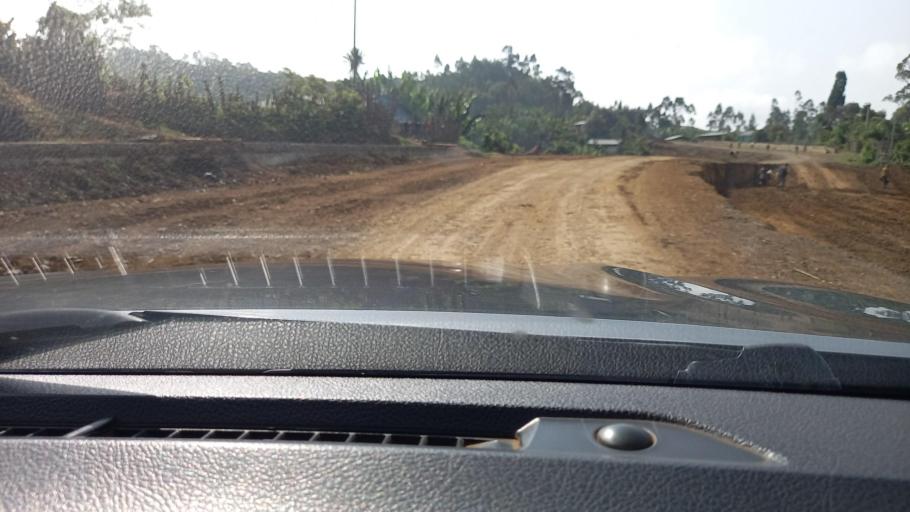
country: ET
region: Southern Nations, Nationalities, and People's Region
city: Mizan Teferi
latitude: 6.1645
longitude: 35.5935
